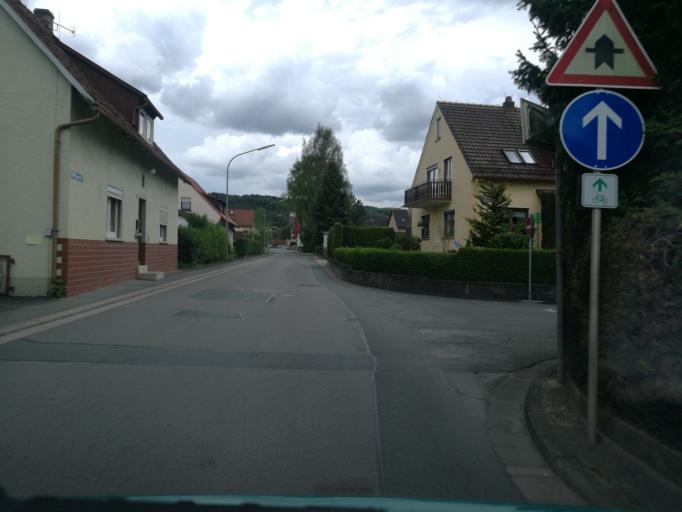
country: DE
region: Bavaria
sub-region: Upper Franconia
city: Weismain
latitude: 50.0900
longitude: 11.2405
